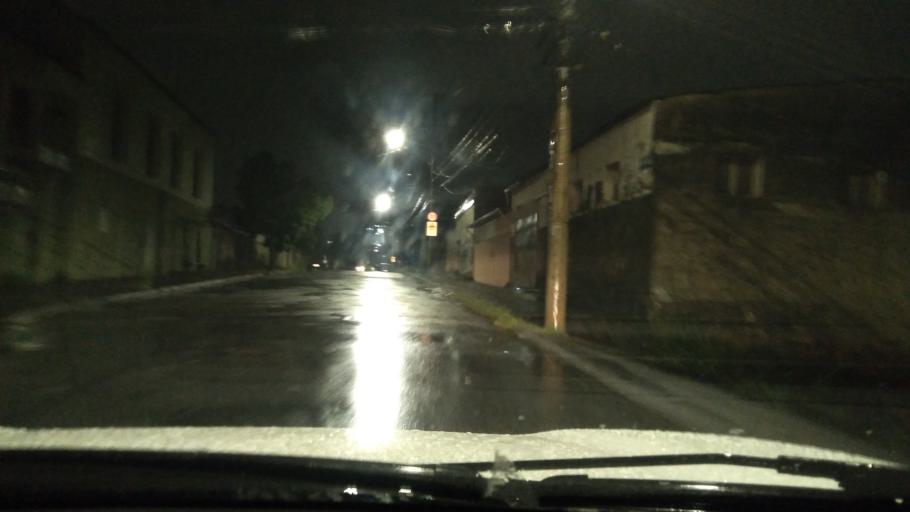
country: BR
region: Minas Gerais
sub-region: Belo Horizonte
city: Belo Horizonte
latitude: -19.8992
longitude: -43.9596
